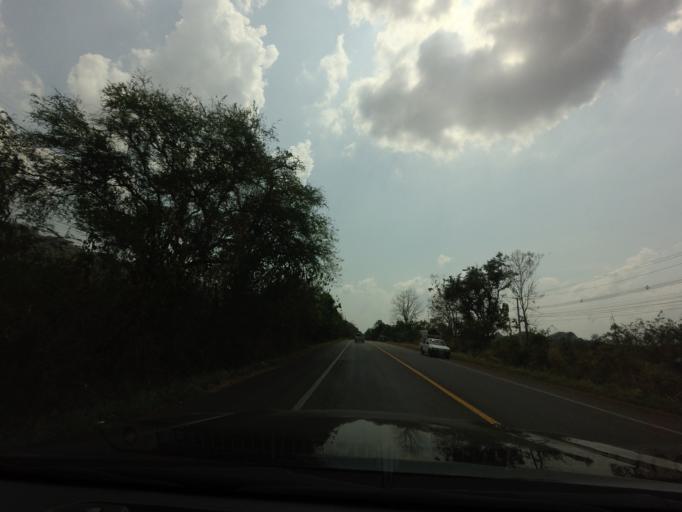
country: TH
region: Kanchanaburi
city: Sai Yok
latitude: 14.1550
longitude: 99.1404
